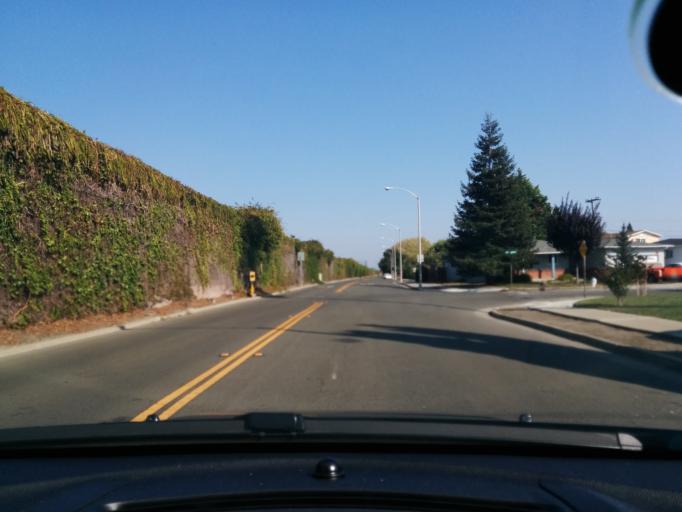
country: US
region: California
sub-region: Santa Clara County
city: Sunnyvale
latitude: 37.3944
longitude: -122.0083
